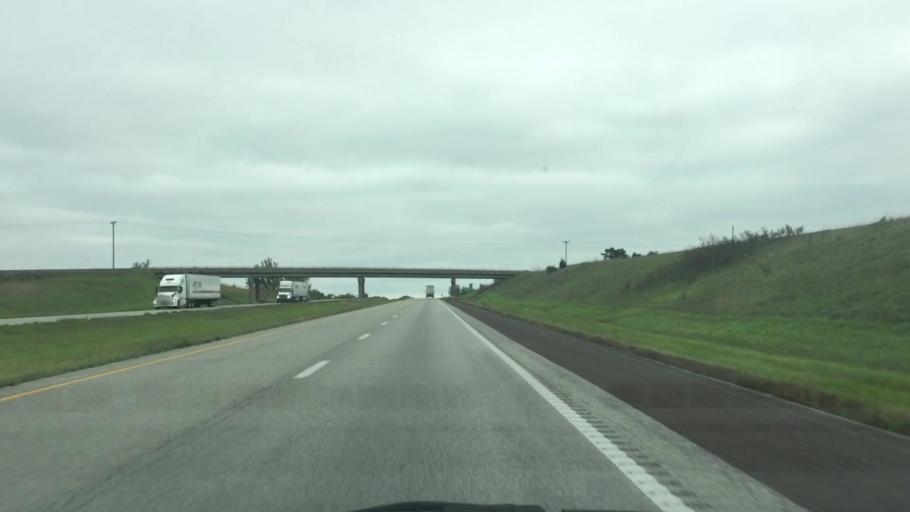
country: US
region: Missouri
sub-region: Daviess County
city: Gallatin
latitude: 39.9303
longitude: -94.1319
